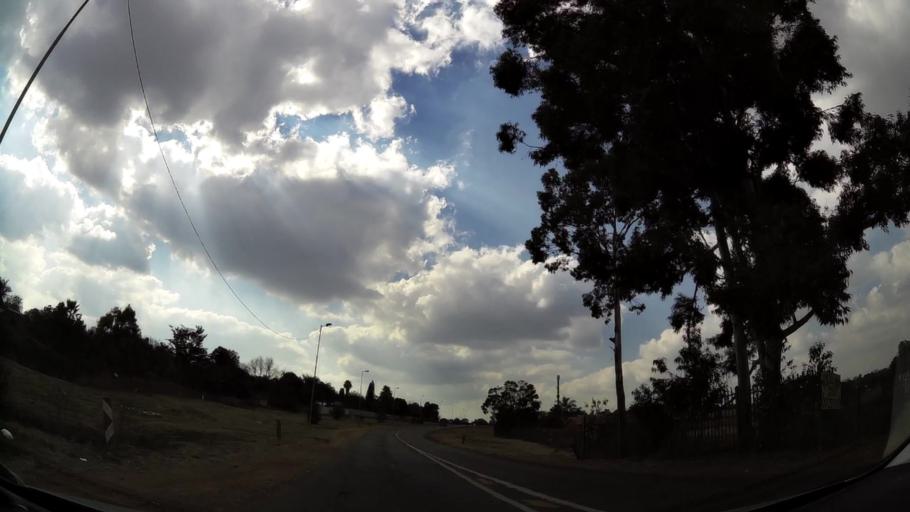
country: ZA
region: Gauteng
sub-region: City of Tshwane Metropolitan Municipality
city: Centurion
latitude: -25.8344
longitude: 28.2529
